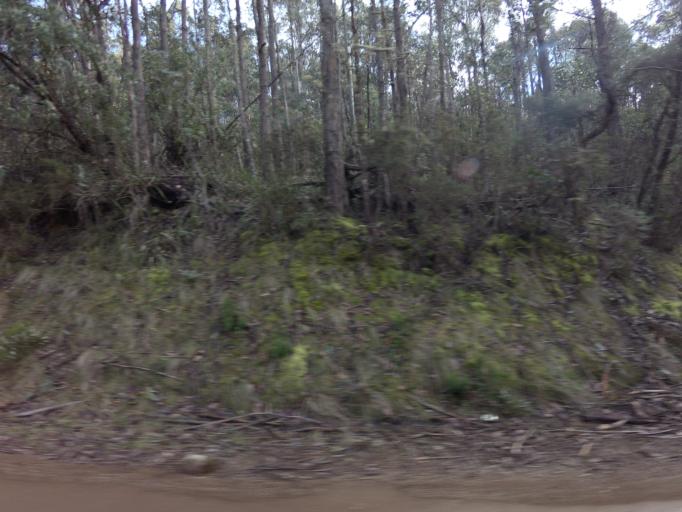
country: AU
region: Tasmania
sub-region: Derwent Valley
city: New Norfolk
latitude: -42.7876
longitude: 146.9360
